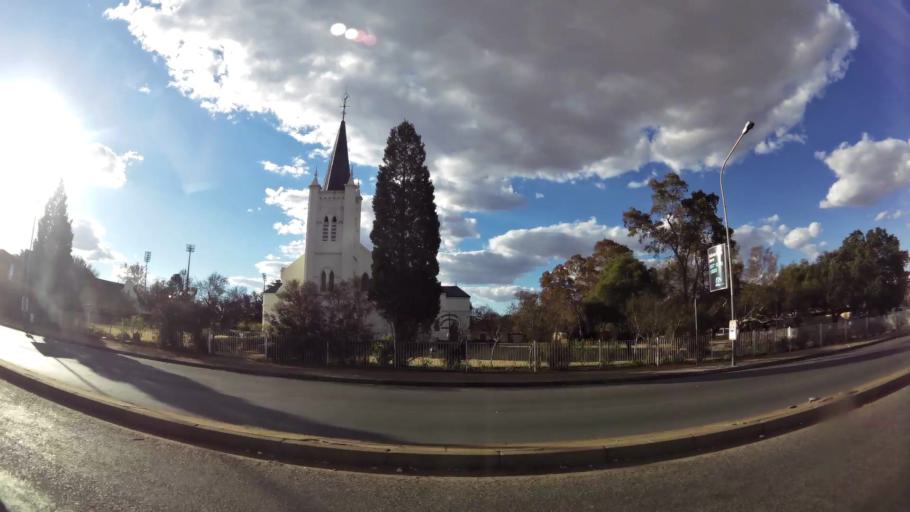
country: ZA
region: North-West
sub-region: Dr Kenneth Kaunda District Municipality
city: Potchefstroom
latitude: -26.7142
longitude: 27.0914
